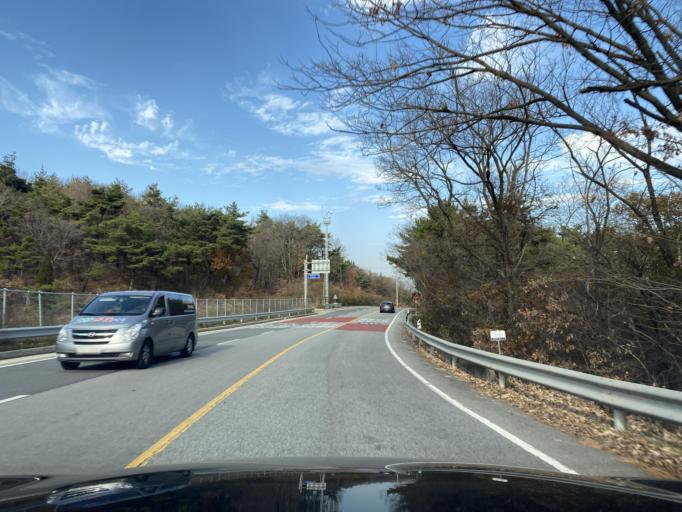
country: KR
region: Chungcheongnam-do
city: Hongsung
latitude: 36.6663
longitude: 126.6365
